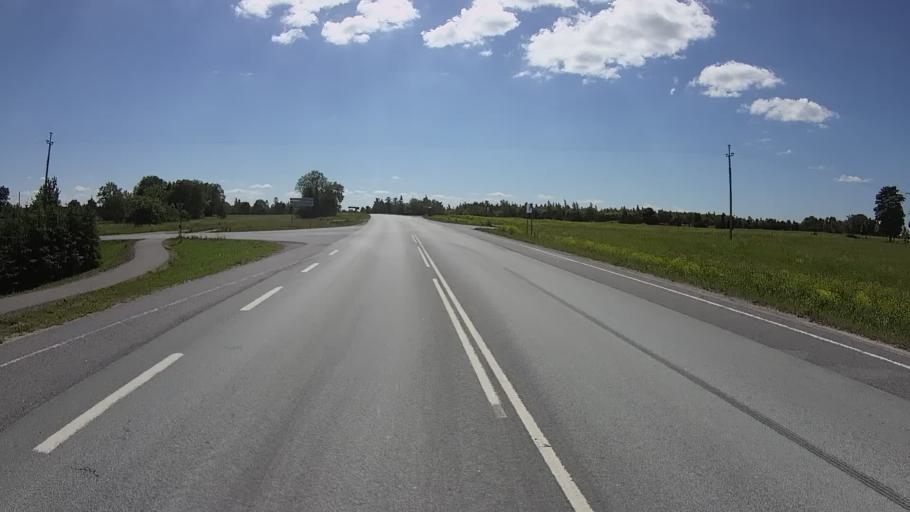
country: EE
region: Laeaene-Virumaa
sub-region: Viru-Nigula vald
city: Kunda
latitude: 59.4810
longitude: 26.4889
